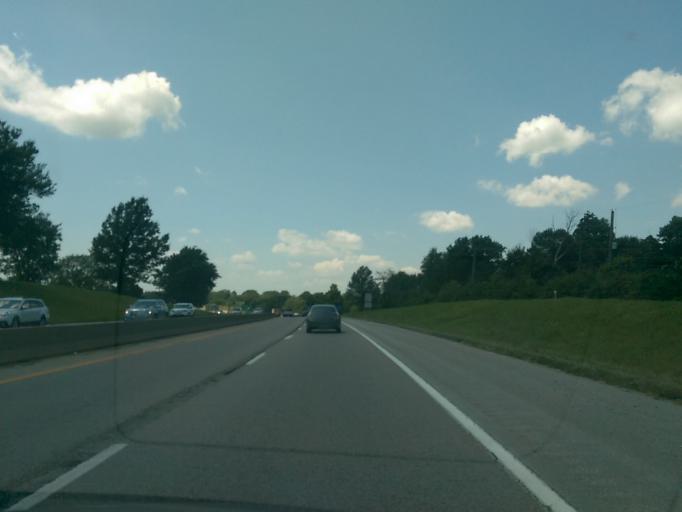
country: US
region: Missouri
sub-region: Boone County
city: Columbia
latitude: 38.9694
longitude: -92.3406
